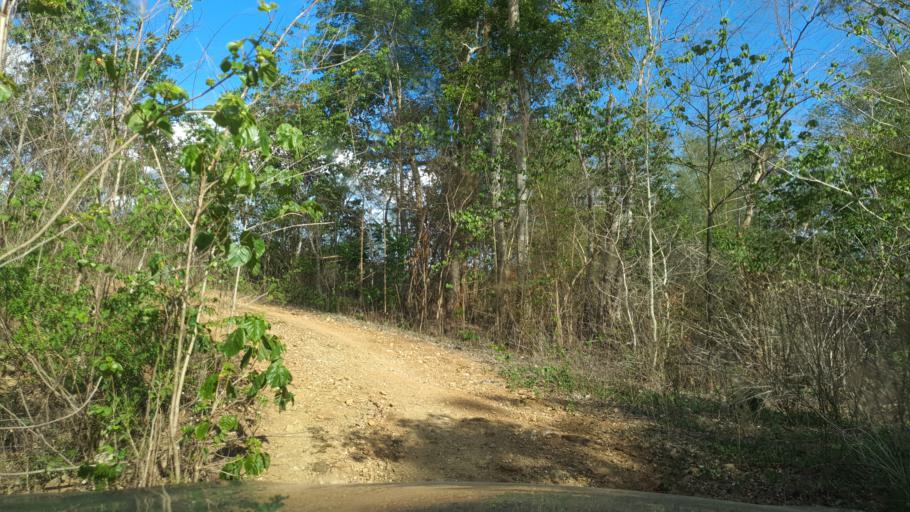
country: TH
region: Lampang
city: Sop Prap
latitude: 17.8382
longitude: 99.2835
